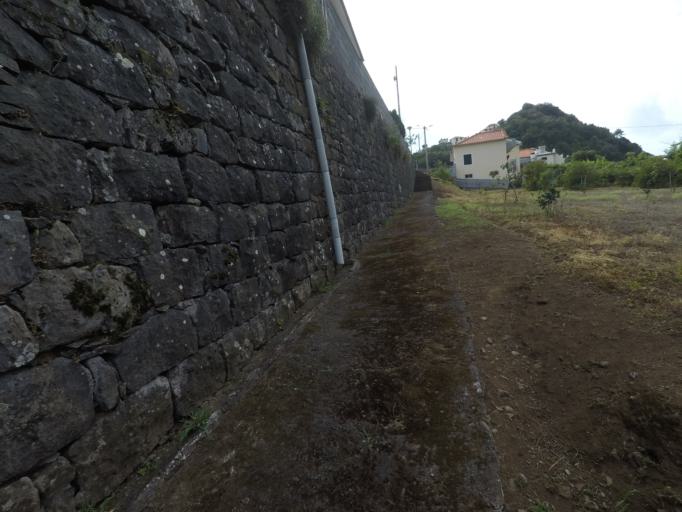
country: PT
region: Madeira
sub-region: Sao Vicente
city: Sao Vicente
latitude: 32.8196
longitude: -16.9703
